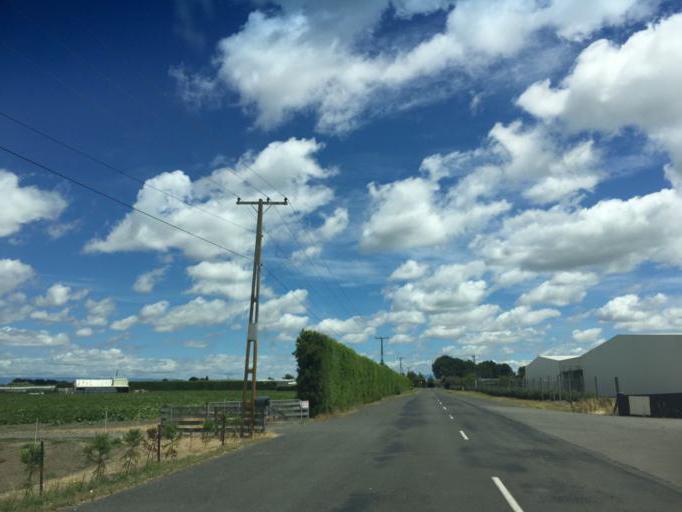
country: NZ
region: Hawke's Bay
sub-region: Hastings District
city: Hastings
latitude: -39.6557
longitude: 176.8903
